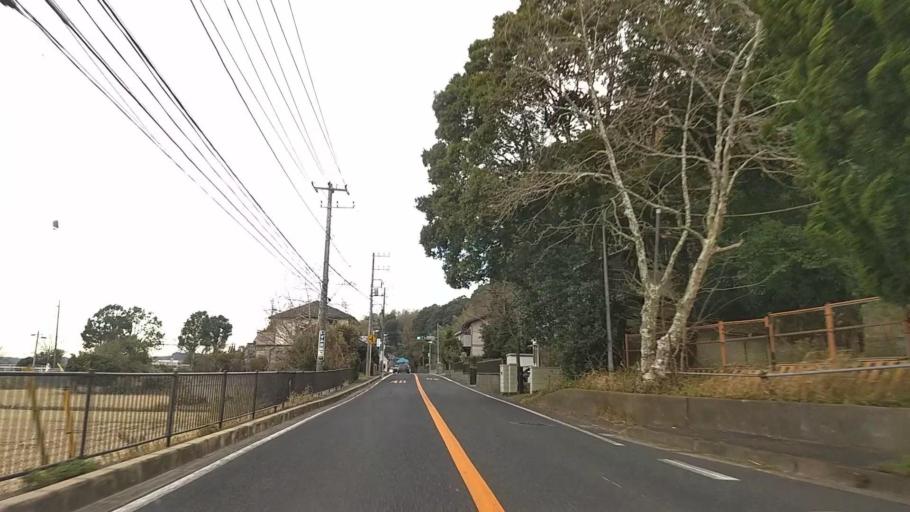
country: JP
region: Chiba
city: Yotsukaido
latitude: 35.6021
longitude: 140.2023
